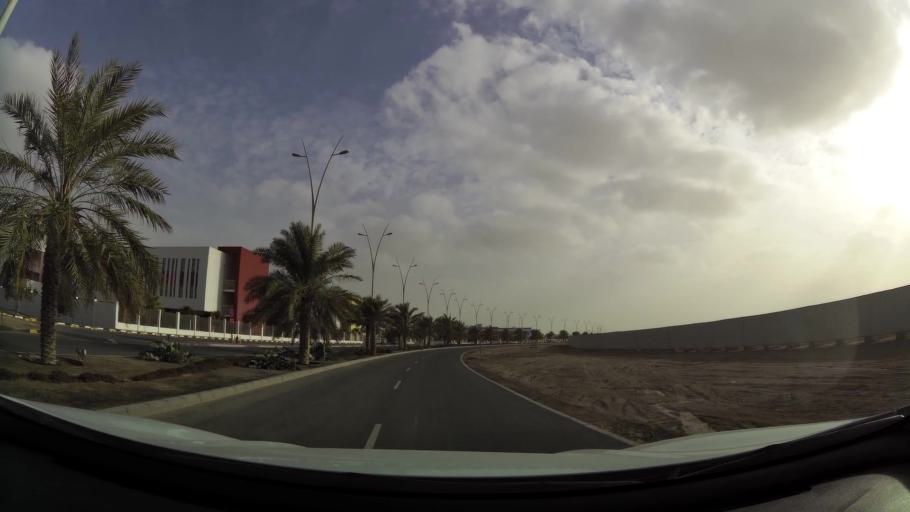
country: AE
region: Abu Dhabi
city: Abu Dhabi
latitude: 24.5100
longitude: 54.5993
